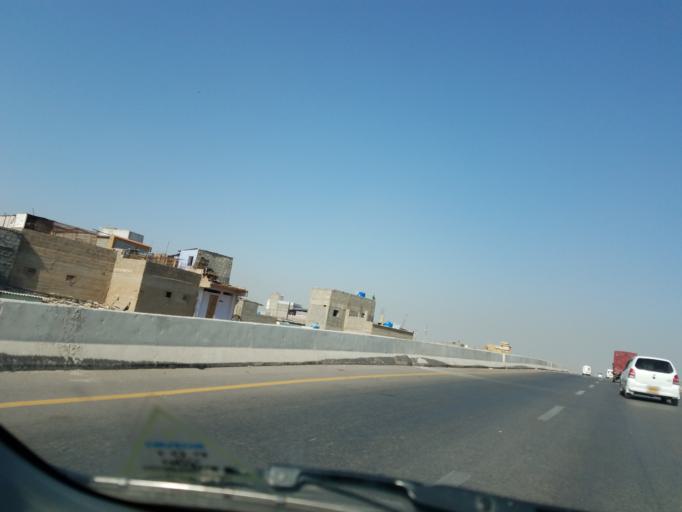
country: PK
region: Sindh
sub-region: Karachi District
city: Karachi
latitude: 24.8838
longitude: 67.0201
